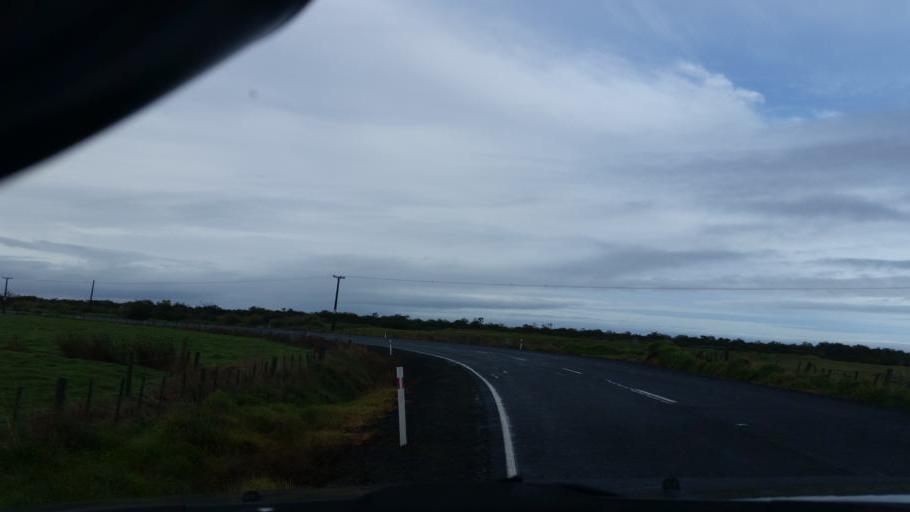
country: NZ
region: Northland
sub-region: Kaipara District
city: Dargaville
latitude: -36.1494
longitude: 174.0664
